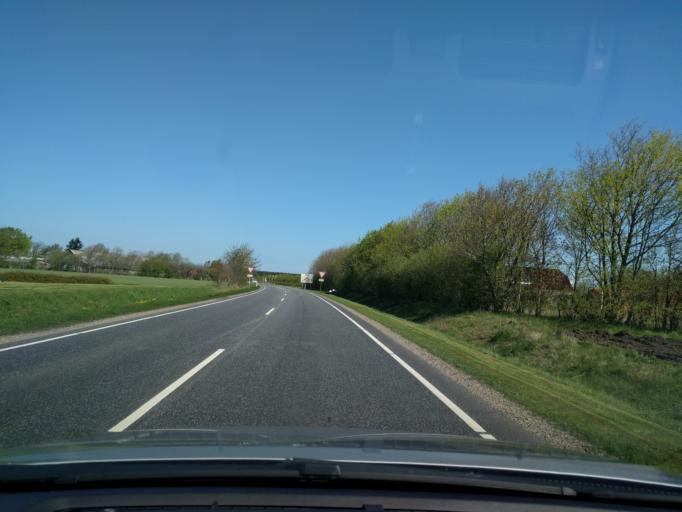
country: DK
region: Central Jutland
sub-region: Ringkobing-Skjern Kommune
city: Videbaek
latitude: 56.0897
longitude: 8.6488
